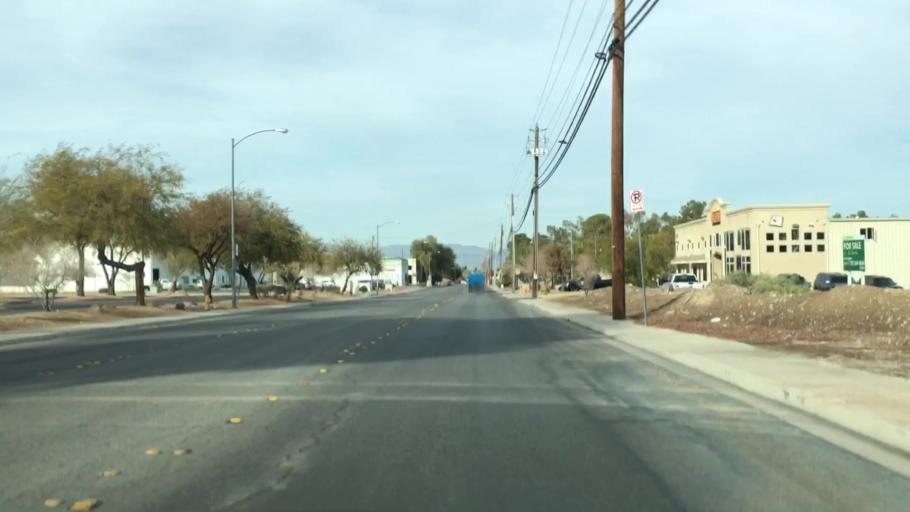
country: US
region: Nevada
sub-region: Clark County
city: Whitney
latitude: 36.0755
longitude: -115.0870
